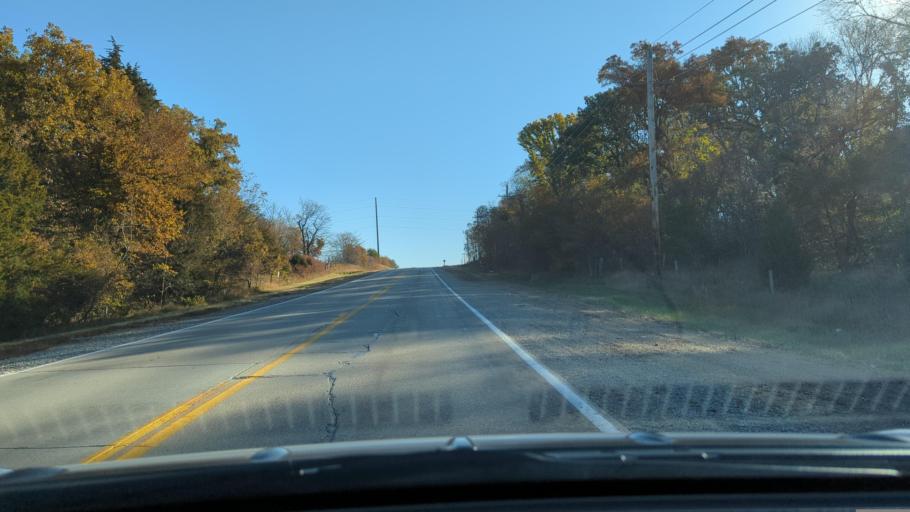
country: US
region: Nebraska
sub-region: Sarpy County
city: Offutt Air Force Base
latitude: 41.0927
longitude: -95.9894
